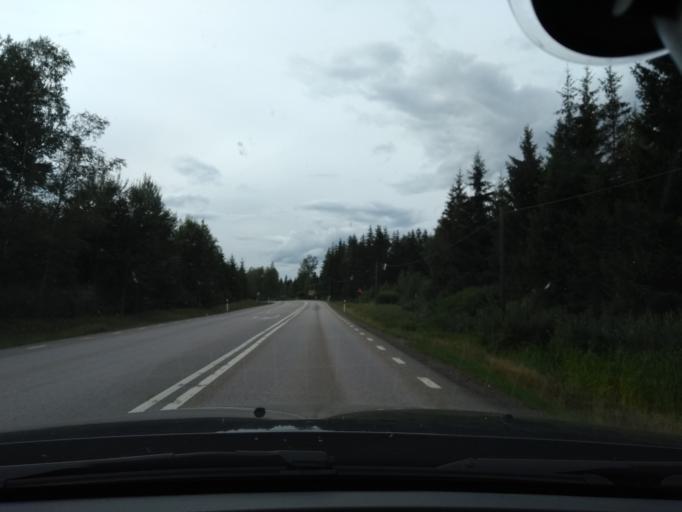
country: SE
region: Joenkoeping
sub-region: Eksjo Kommun
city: Mariannelund
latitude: 57.6348
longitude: 15.6278
